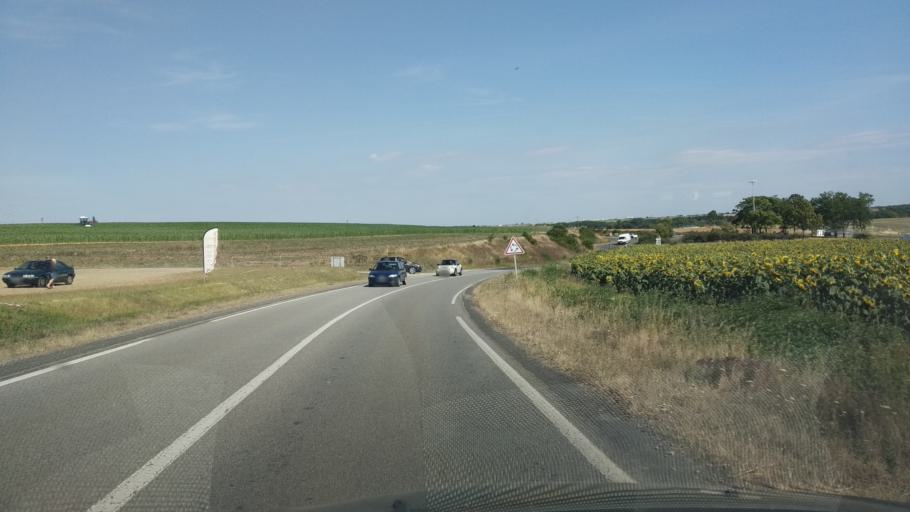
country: FR
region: Poitou-Charentes
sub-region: Departement de la Vienne
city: Cisse
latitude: 46.6306
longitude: 0.2614
